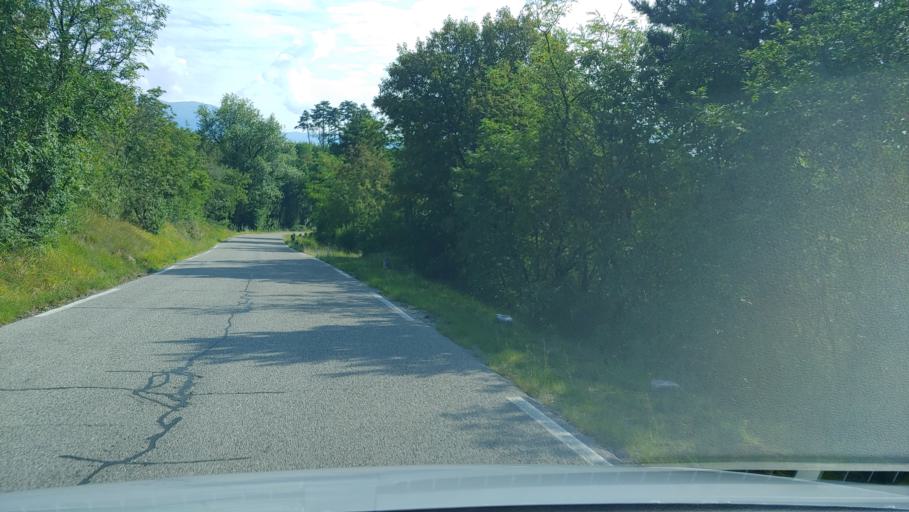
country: SI
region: Komen
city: Komen
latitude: 45.8462
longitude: 13.7821
